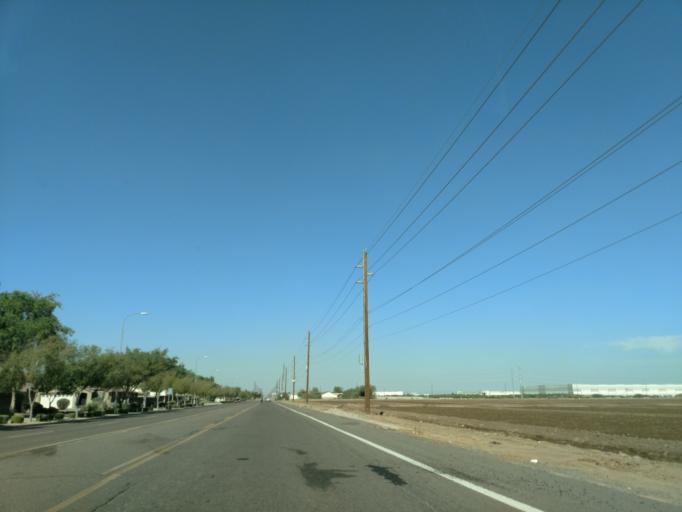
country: US
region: Arizona
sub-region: Maricopa County
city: Laveen
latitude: 33.4100
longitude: -112.1865
